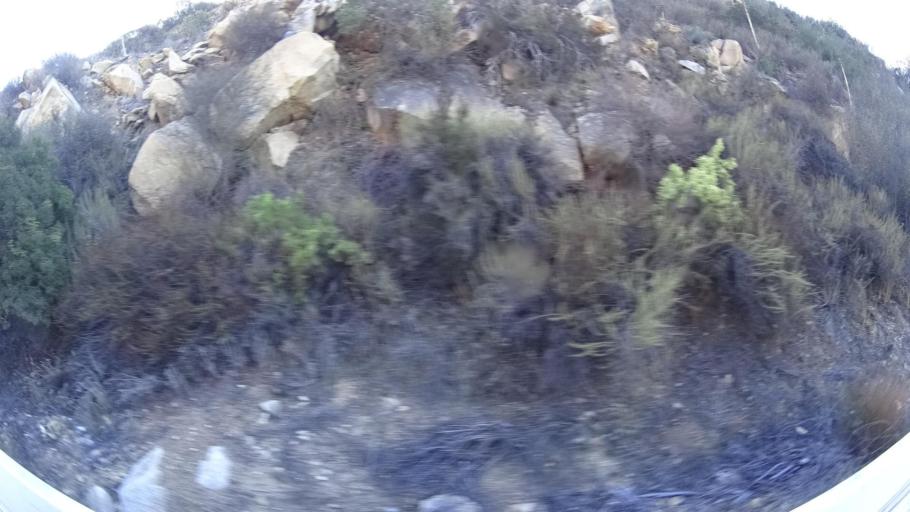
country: US
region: California
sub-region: San Diego County
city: Jamul
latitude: 32.6726
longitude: -116.7602
